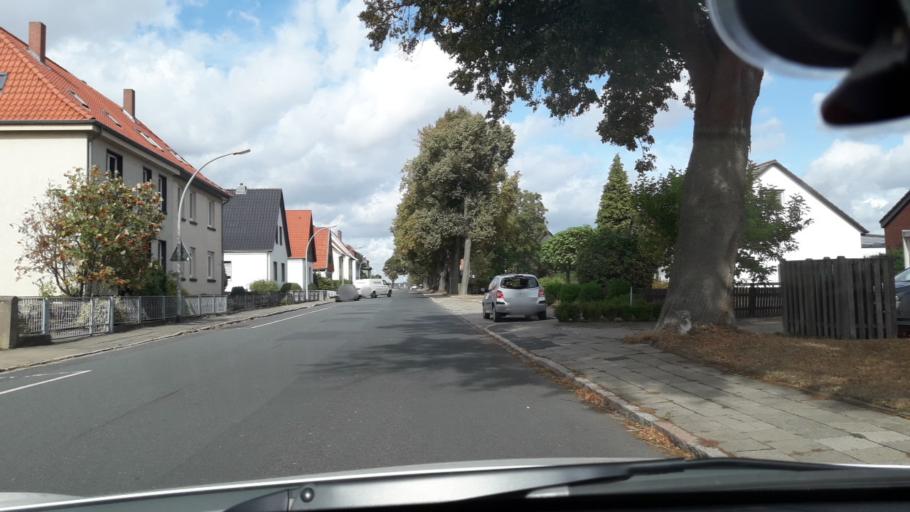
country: DE
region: Lower Saxony
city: Alt Wallmoden
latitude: 52.0403
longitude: 10.3121
